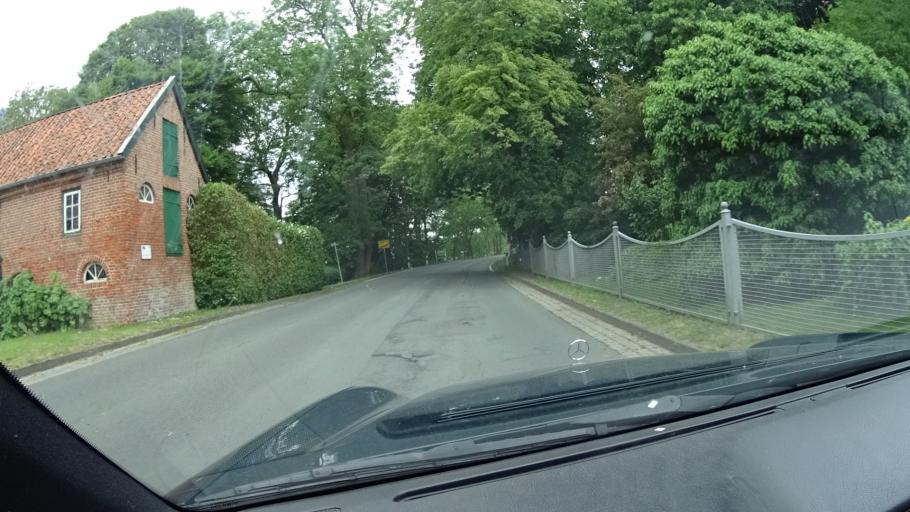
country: DE
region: Lower Saxony
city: Butjadingen
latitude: 53.5933
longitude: 8.2790
